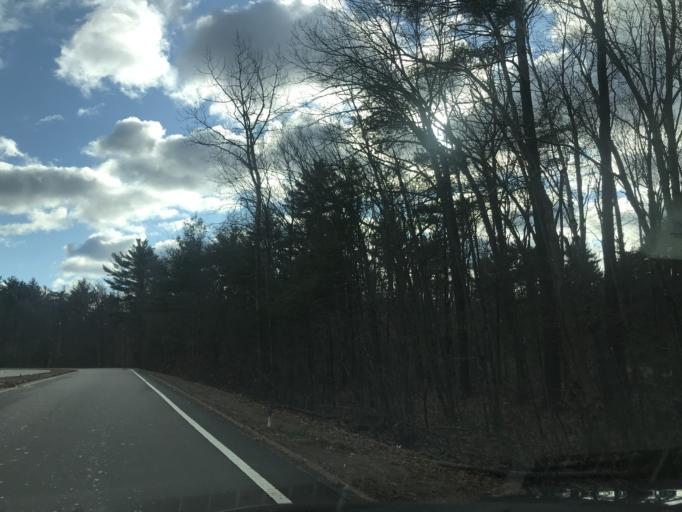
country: US
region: Massachusetts
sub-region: Plymouth County
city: Hanover
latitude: 42.1513
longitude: -70.8482
